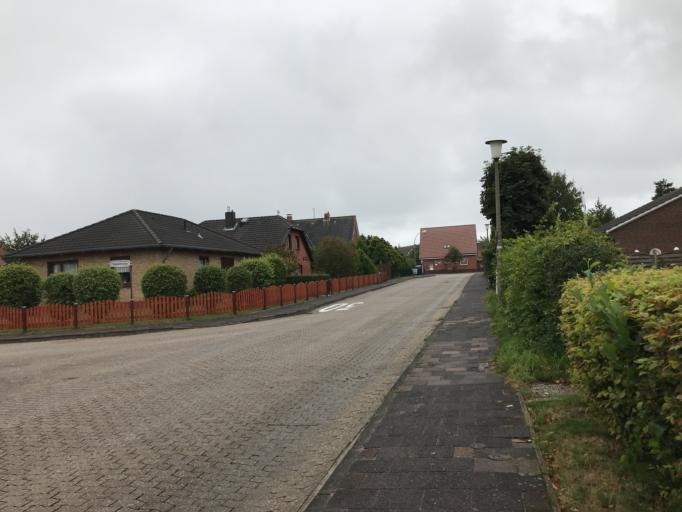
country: DE
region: Lower Saxony
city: Borkum
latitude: 53.5829
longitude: 6.6823
